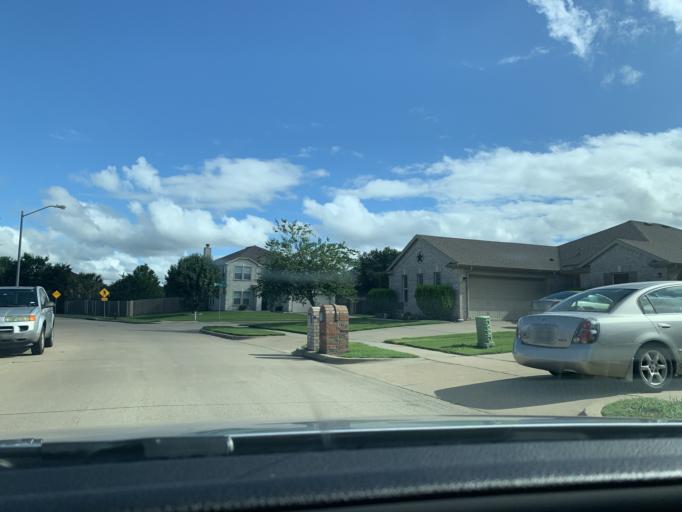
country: US
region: Texas
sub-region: Dallas County
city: Cedar Hill
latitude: 32.6439
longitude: -97.0369
